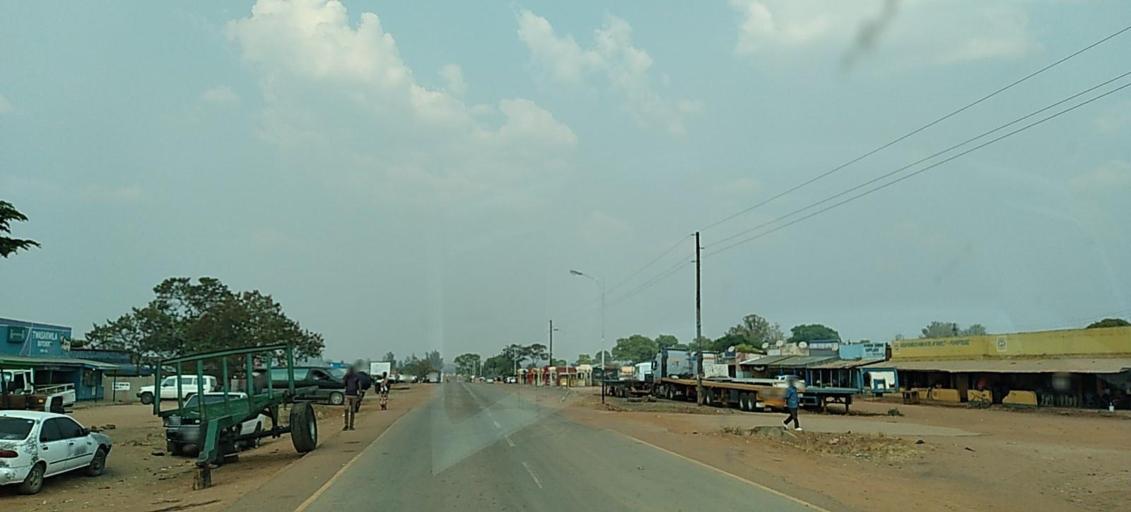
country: ZM
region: North-Western
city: Kabompo
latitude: -13.5941
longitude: 24.1990
